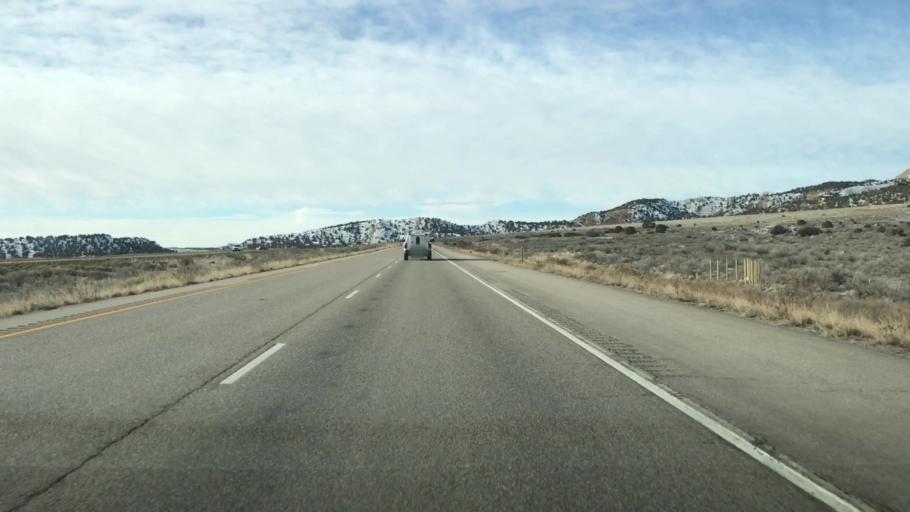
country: US
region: Colorado
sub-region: Garfield County
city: Parachute
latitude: 39.3867
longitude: -108.1446
